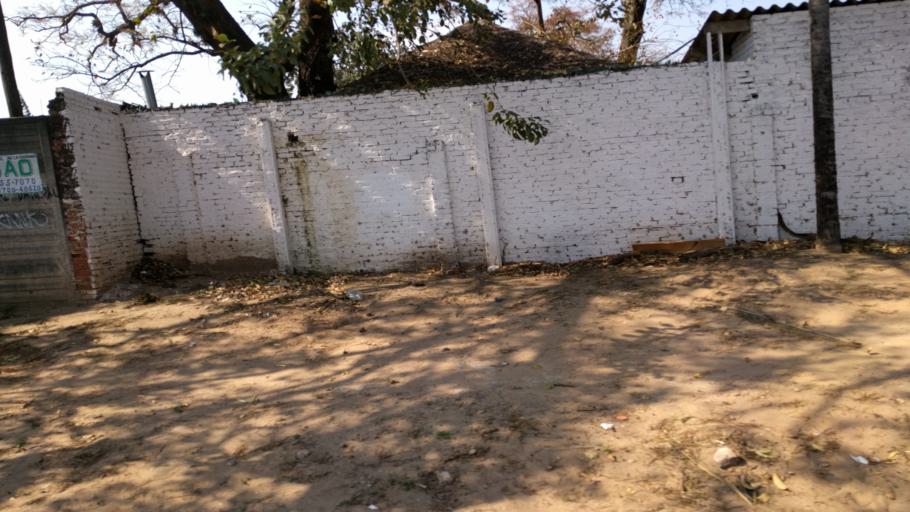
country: BO
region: Santa Cruz
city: Santa Cruz de la Sierra
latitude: -17.8098
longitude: -63.1679
